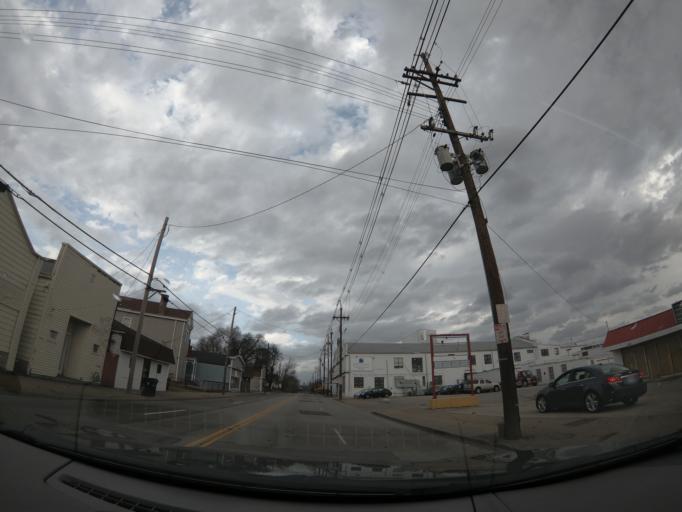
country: US
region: Kentucky
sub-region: Jefferson County
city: Louisville
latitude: 38.2272
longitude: -85.7688
